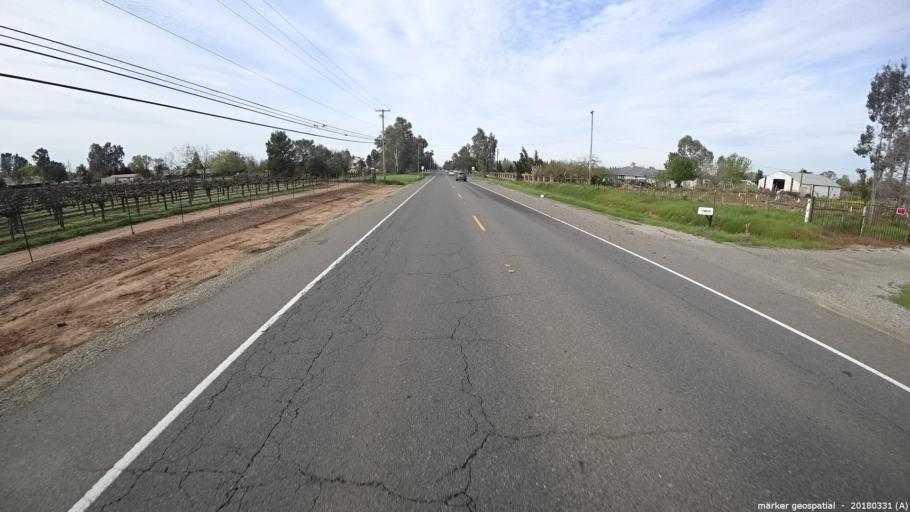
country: US
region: California
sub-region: Sacramento County
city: Wilton
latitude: 38.4470
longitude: -121.2827
